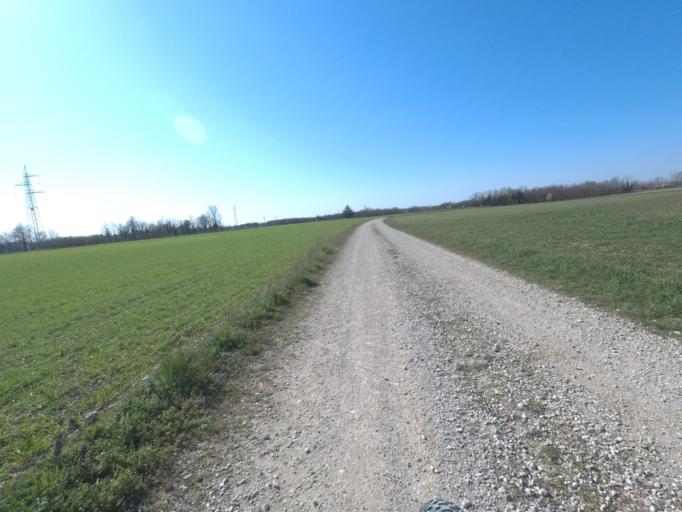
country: IT
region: Friuli Venezia Giulia
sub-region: Provincia di Udine
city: Pradamano
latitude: 46.0624
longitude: 13.3054
